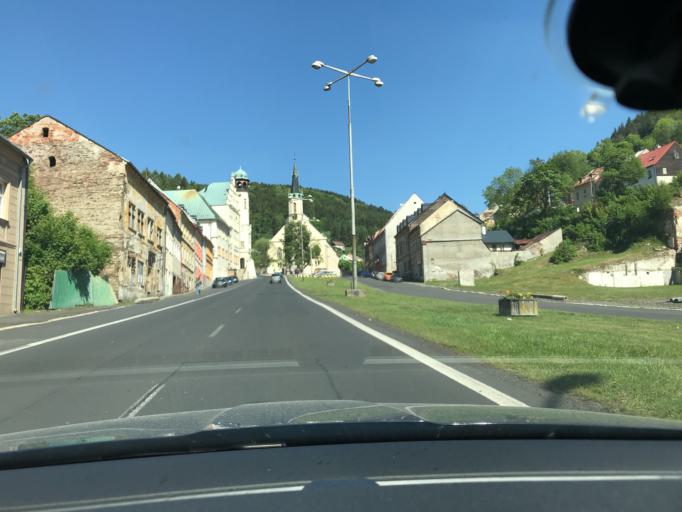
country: CZ
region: Karlovarsky
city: Jachymov
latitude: 50.3703
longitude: 12.9154
